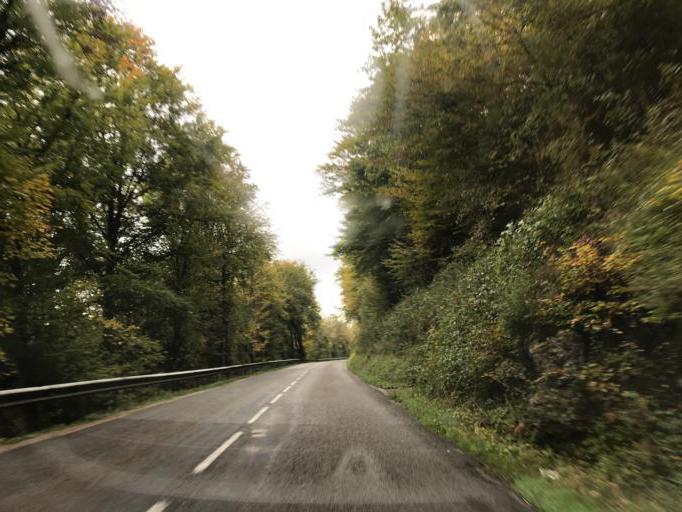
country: FR
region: Franche-Comte
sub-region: Departement du Jura
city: Orgelet
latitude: 46.4812
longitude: 5.5831
